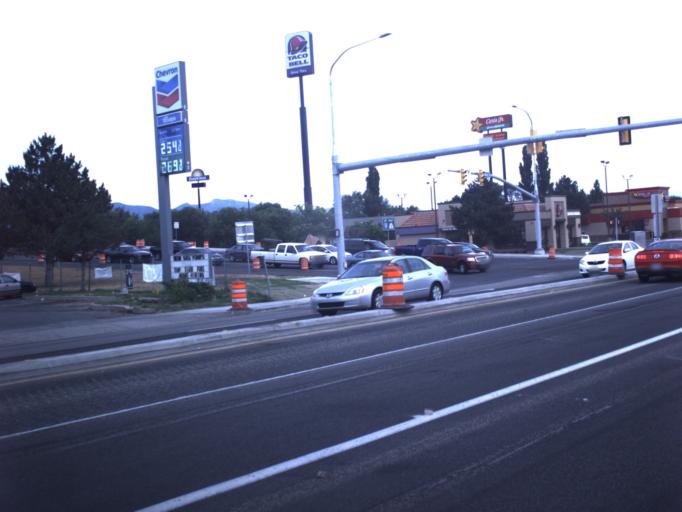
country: US
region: Utah
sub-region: Davis County
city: Clearfield
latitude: 41.1236
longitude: -112.0261
